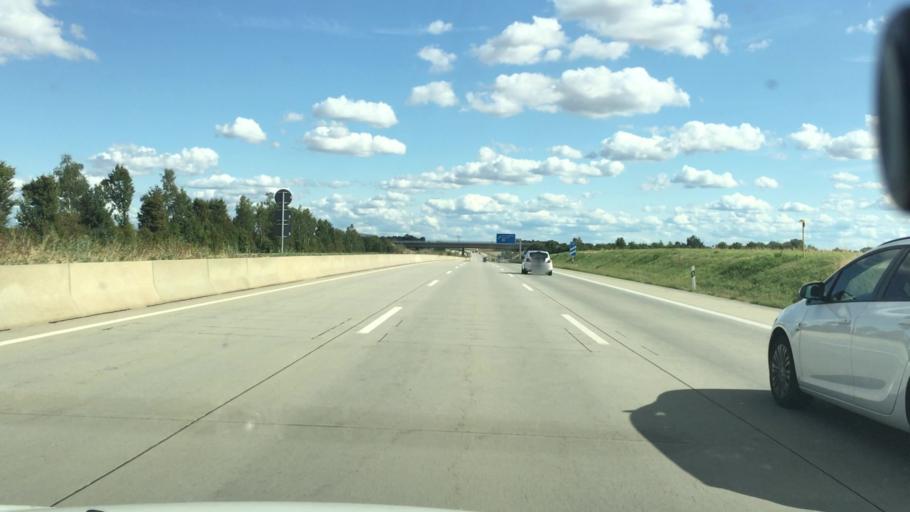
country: DE
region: Thuringia
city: Schwaara
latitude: 50.8890
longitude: 12.1469
